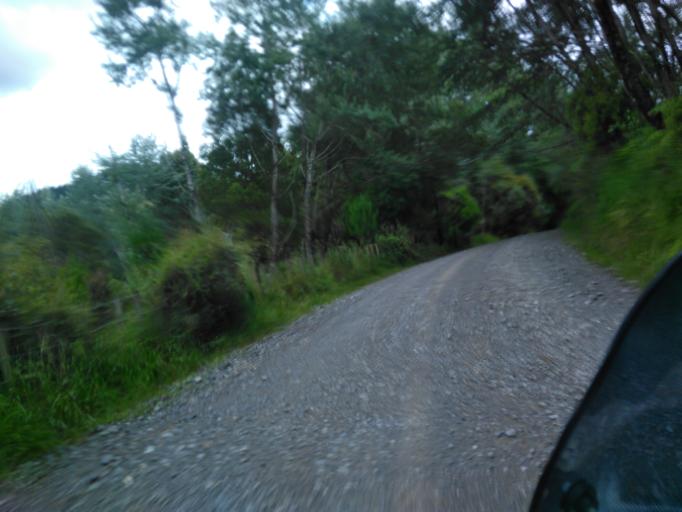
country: NZ
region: Gisborne
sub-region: Gisborne District
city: Gisborne
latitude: -38.0816
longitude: 178.0512
